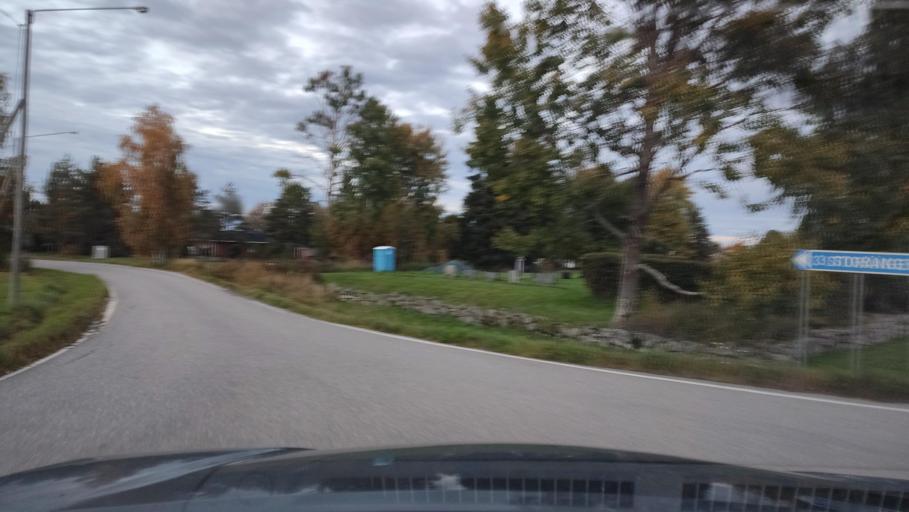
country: FI
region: Ostrobothnia
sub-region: Sydosterbotten
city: Kristinestad
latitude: 62.2548
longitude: 21.5108
